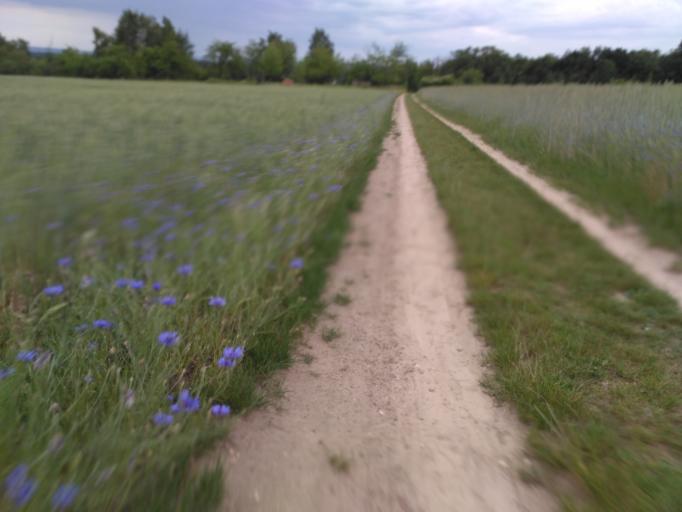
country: DE
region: Brandenburg
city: Hohenleipisch
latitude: 51.4942
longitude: 13.5254
